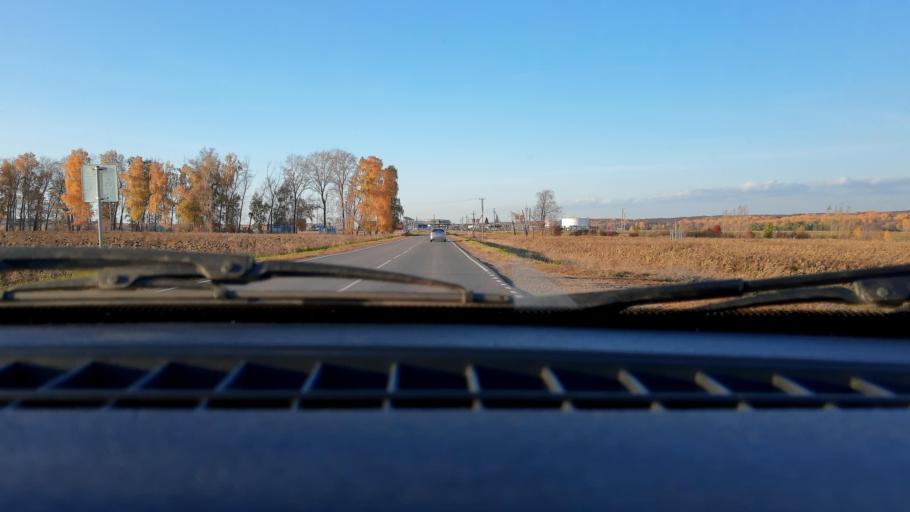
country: RU
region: Bashkortostan
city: Mikhaylovka
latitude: 54.8200
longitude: 55.7666
